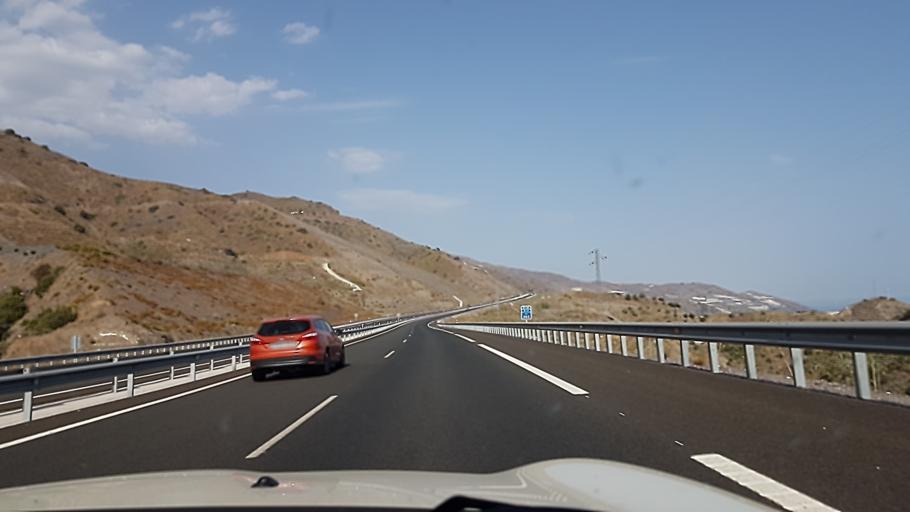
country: ES
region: Andalusia
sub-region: Provincia de Granada
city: Sorvilan
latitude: 36.7515
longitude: -3.2806
